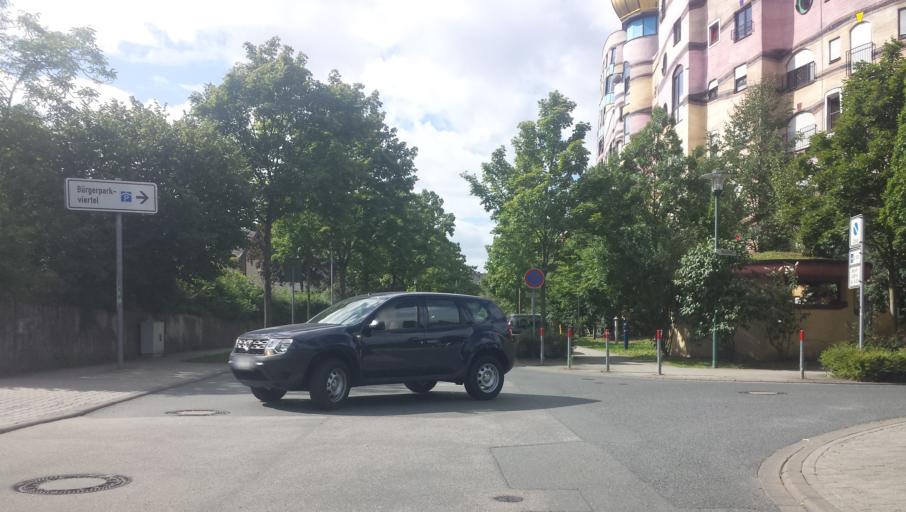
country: DE
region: Hesse
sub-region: Regierungsbezirk Darmstadt
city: Darmstadt
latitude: 49.8860
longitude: 8.6566
